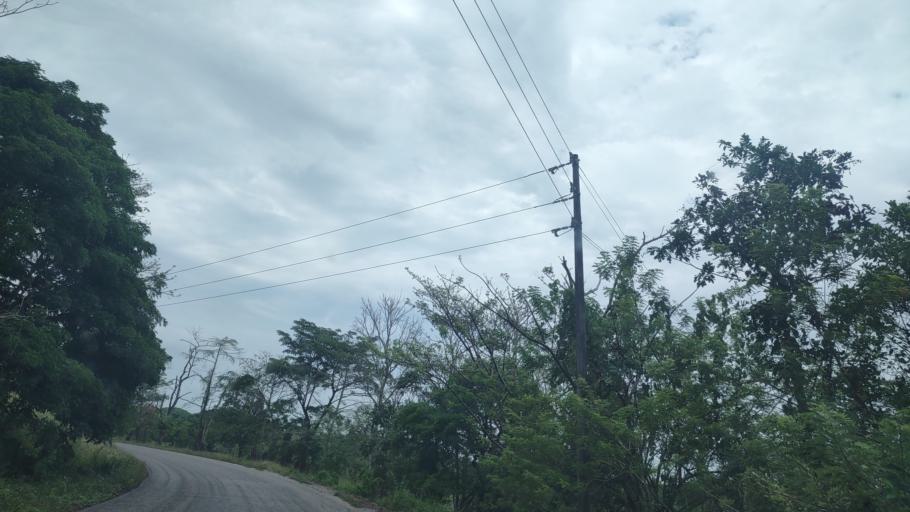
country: MX
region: Tabasco
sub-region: Huimanguillo
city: Francisco Rueda
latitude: 17.5393
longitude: -94.1258
